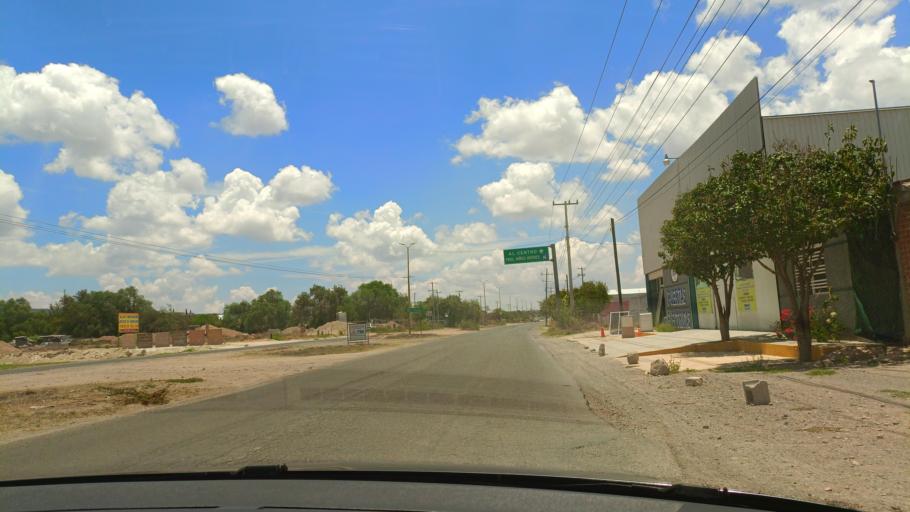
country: MX
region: Guanajuato
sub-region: San Luis de la Paz
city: San Ignacio
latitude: 21.2874
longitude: -100.5524
